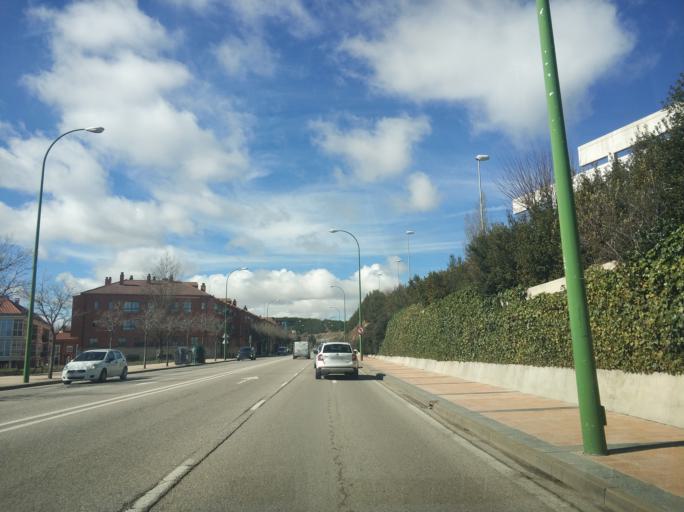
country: ES
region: Castille and Leon
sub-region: Provincia de Burgos
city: Burgos
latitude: 42.3606
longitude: -3.6855
